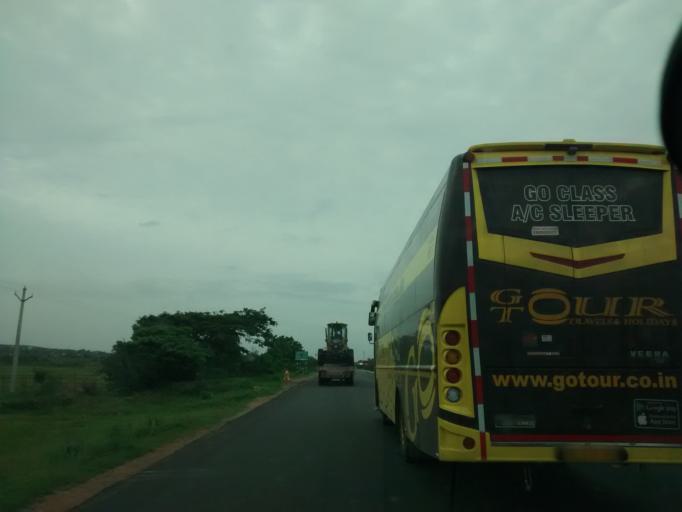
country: IN
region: Telangana
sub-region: Mahbubnagar
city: Wanparti
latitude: 16.3294
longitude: 77.9496
